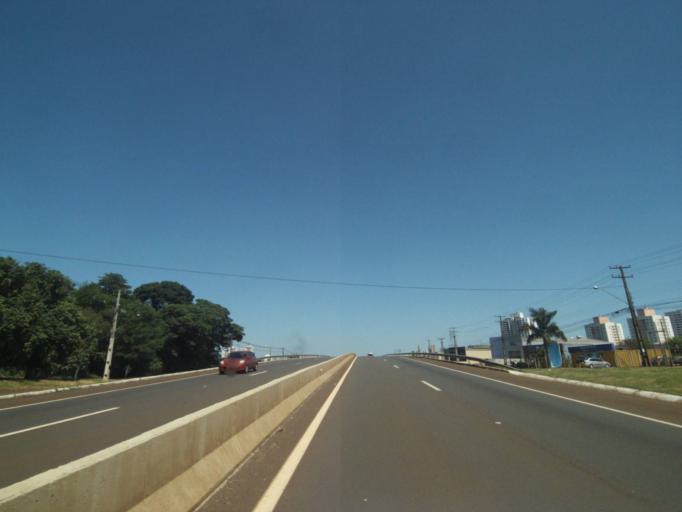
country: BR
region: Parana
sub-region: Londrina
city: Londrina
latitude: -23.3486
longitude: -51.1693
